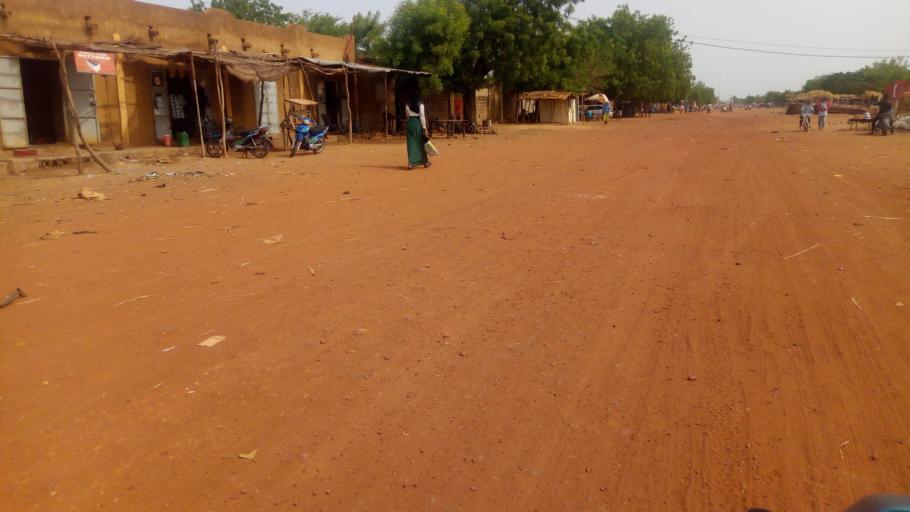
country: ML
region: Segou
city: Segou
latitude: 13.4267
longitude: -6.2599
